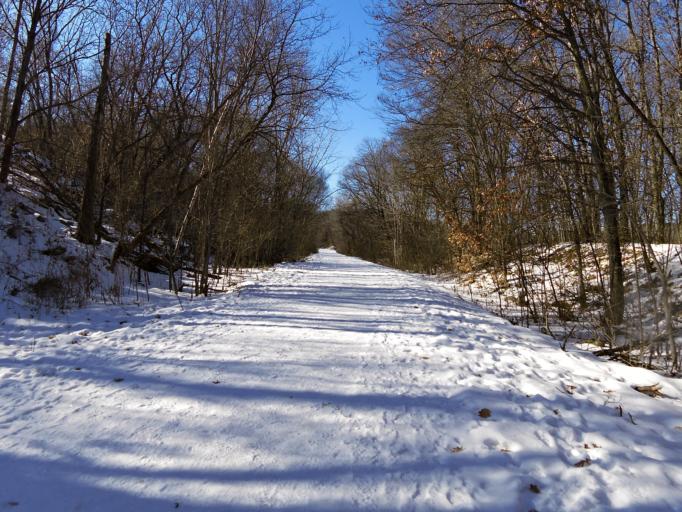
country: US
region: Minnesota
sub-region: Washington County
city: Stillwater
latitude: 45.0748
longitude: -92.8098
